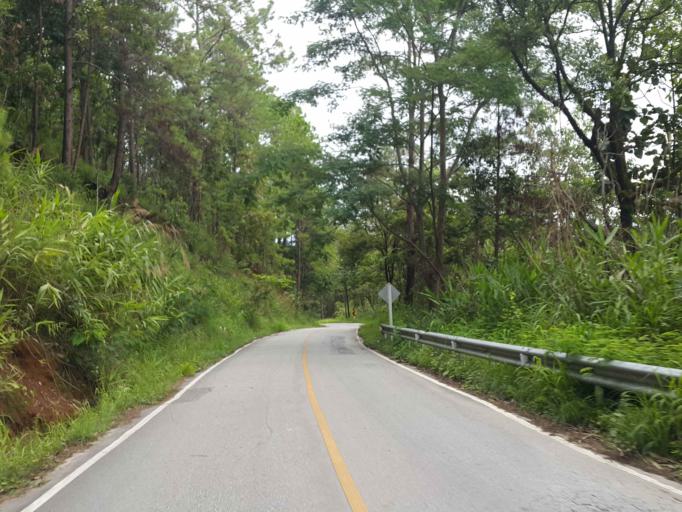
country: TH
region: Chiang Mai
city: Mae Chaem
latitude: 18.5154
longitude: 98.4467
